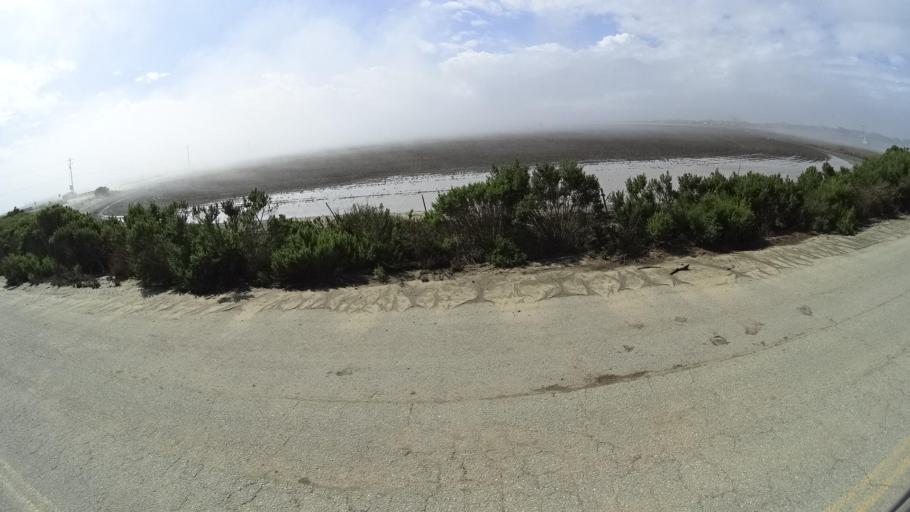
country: US
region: California
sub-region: Monterey County
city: Castroville
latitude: 36.7695
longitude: -121.7911
